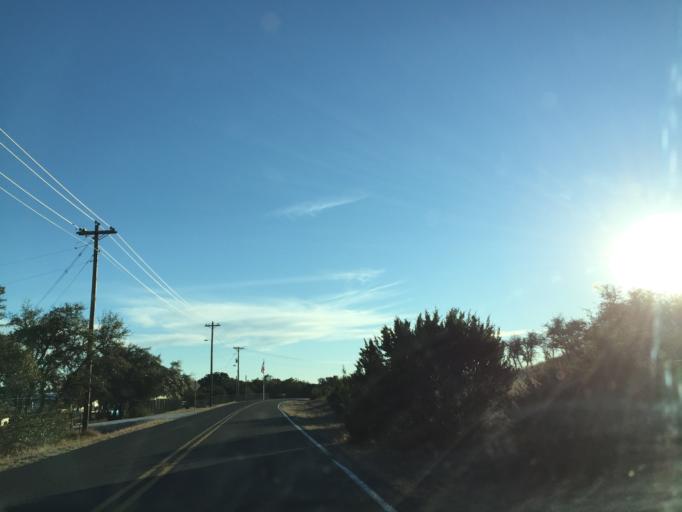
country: US
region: Texas
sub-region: Travis County
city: Lago Vista
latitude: 30.5005
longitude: -98.0583
